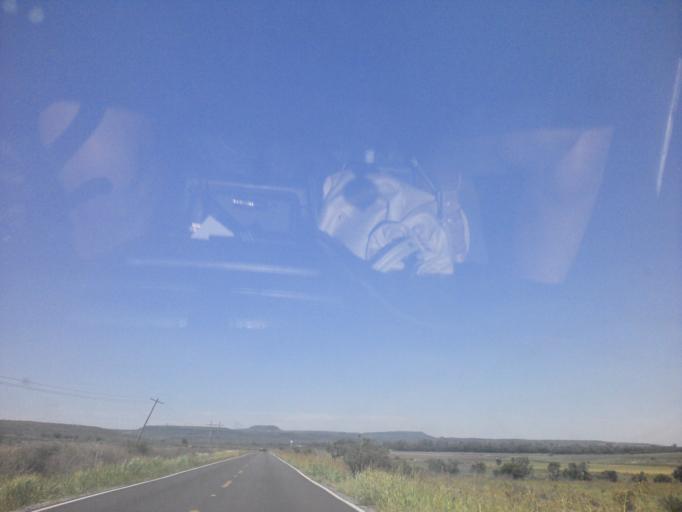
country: MX
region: Guanajuato
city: Ciudad Manuel Doblado
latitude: 20.8571
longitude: -101.9975
